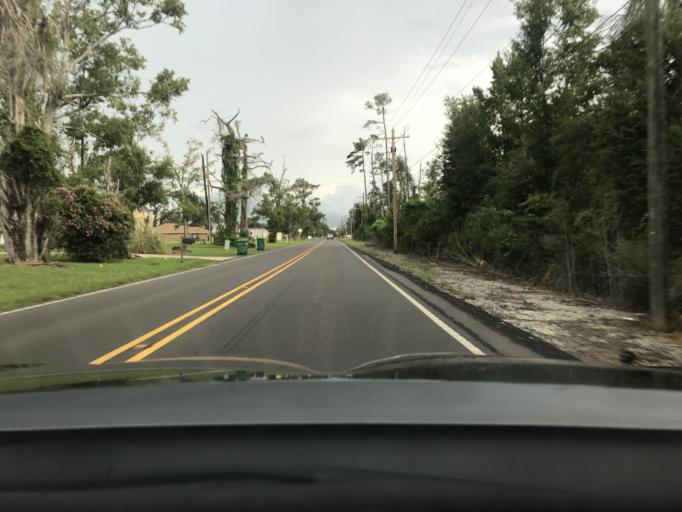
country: US
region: Louisiana
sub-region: Calcasieu Parish
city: Westlake
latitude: 30.2537
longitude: -93.2455
